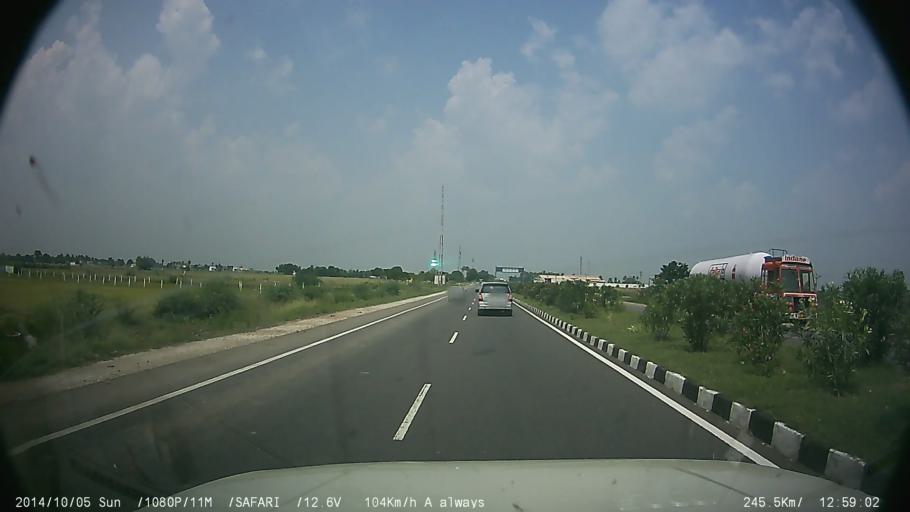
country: IN
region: Tamil Nadu
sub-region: Cuddalore
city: Panruti
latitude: 11.8101
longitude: 79.4159
